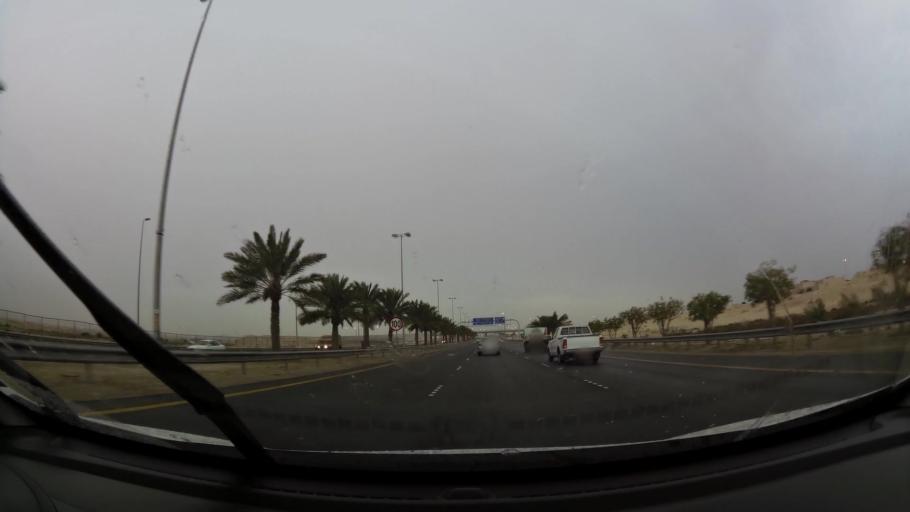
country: BH
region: Central Governorate
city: Dar Kulayb
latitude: 26.0872
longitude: 50.5153
